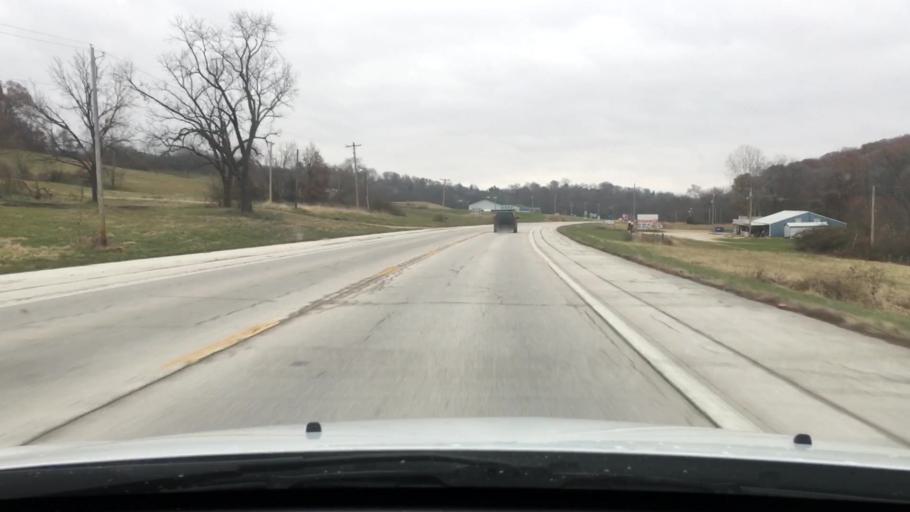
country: US
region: Missouri
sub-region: Pike County
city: Louisiana
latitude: 39.4492
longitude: -91.0705
